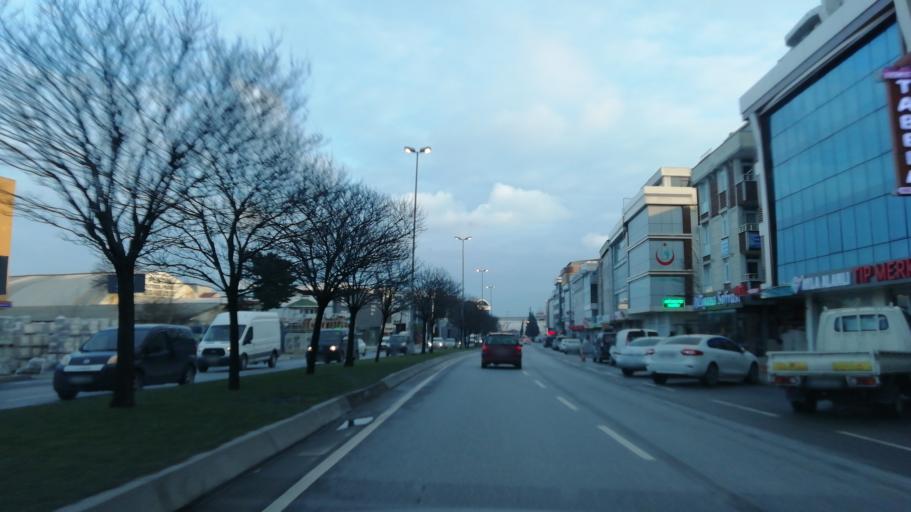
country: TR
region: Istanbul
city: Yakuplu
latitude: 41.0024
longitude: 28.7103
